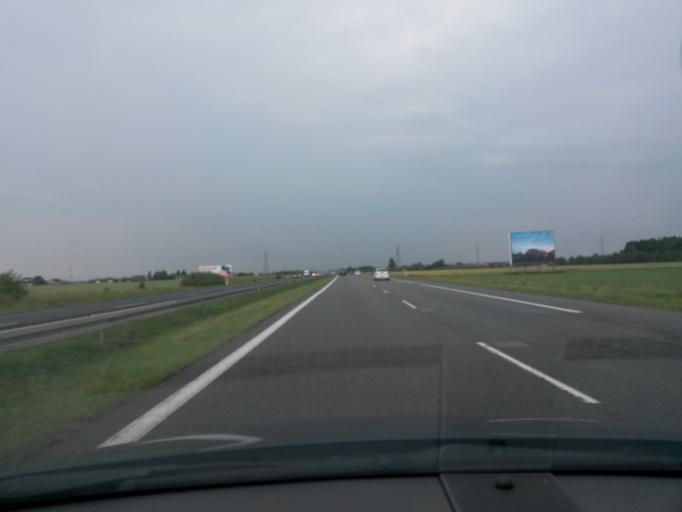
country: PL
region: Lodz Voivodeship
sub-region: Powiat piotrkowski
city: Wola Krzysztoporska
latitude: 51.3900
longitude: 19.6284
